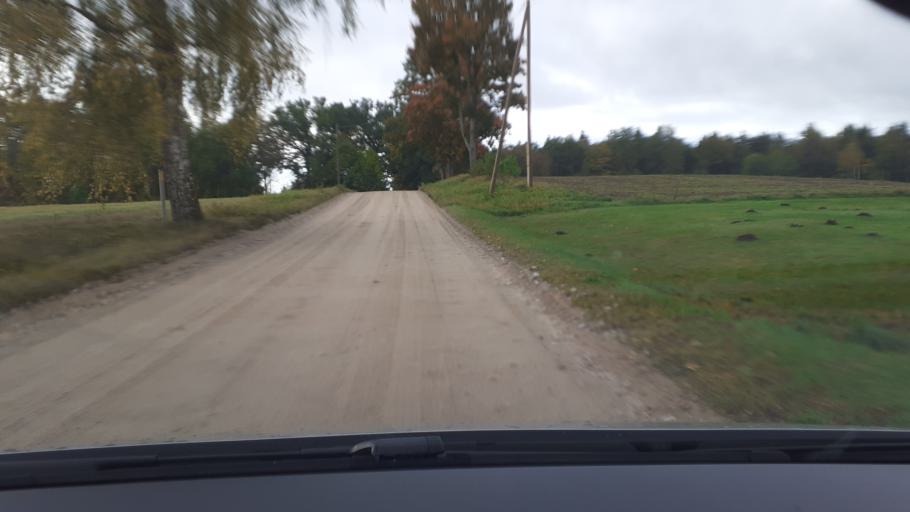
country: LV
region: Kuldigas Rajons
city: Kuldiga
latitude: 57.0265
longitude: 21.9147
